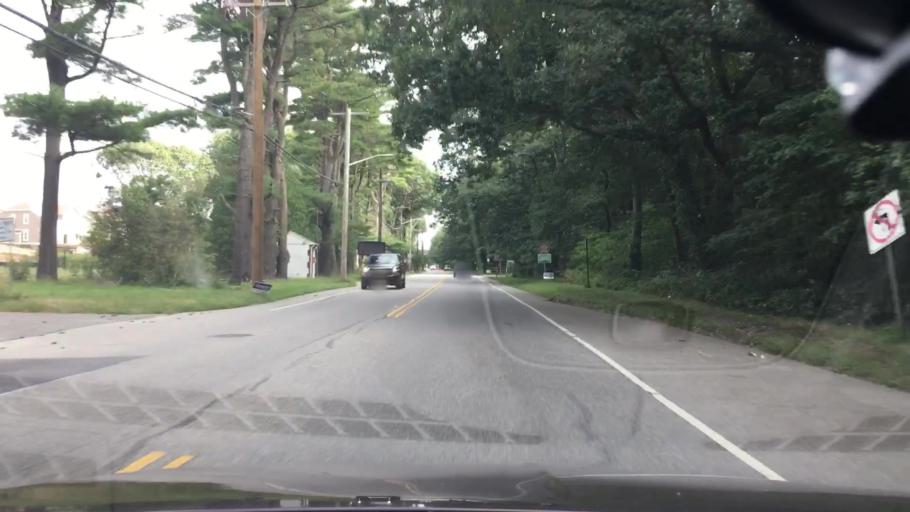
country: US
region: New York
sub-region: Nassau County
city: Old Bethpage
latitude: 40.7739
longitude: -73.4483
